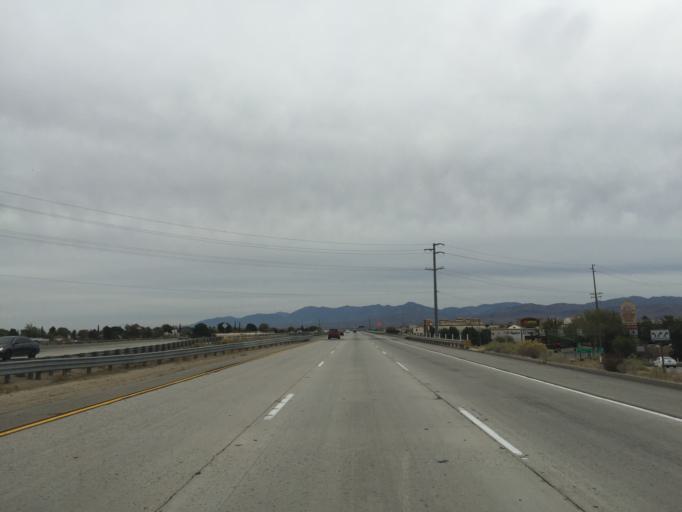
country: US
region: California
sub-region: Los Angeles County
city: Desert View Highlands
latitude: 34.6064
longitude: -118.1491
